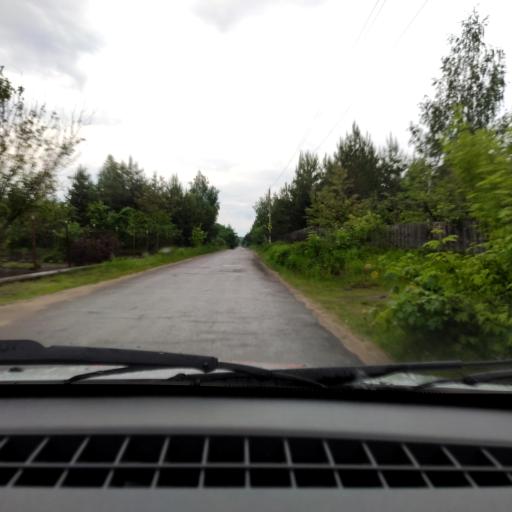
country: RU
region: Voronezj
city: Ramon'
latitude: 51.8518
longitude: 39.2400
